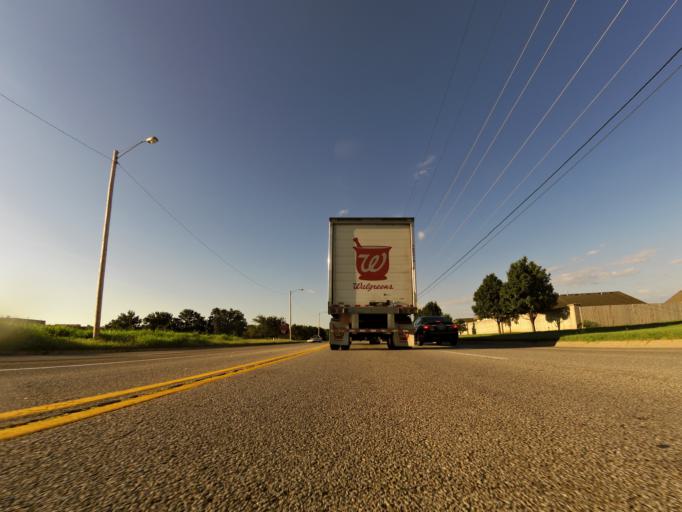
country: US
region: Kansas
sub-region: Sedgwick County
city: Bellaire
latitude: 37.7328
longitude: -97.2624
